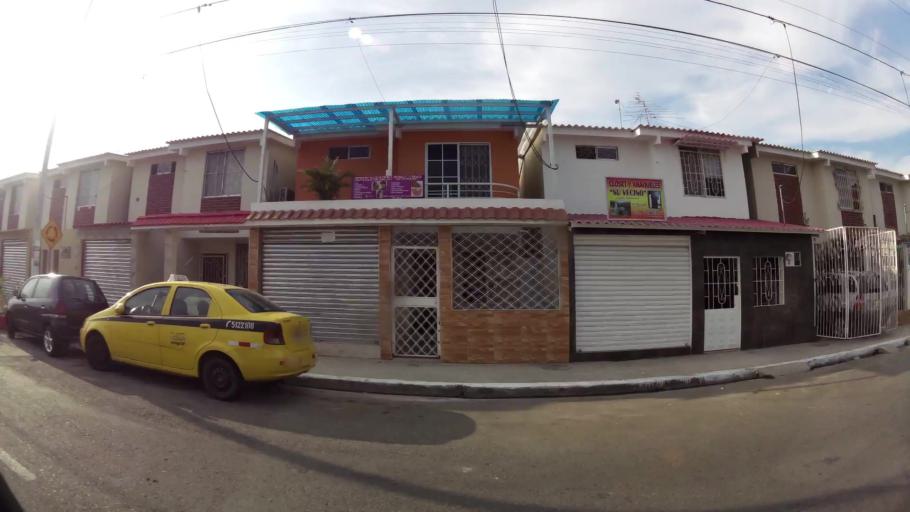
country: EC
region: Guayas
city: Eloy Alfaro
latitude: -2.0651
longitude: -79.8954
